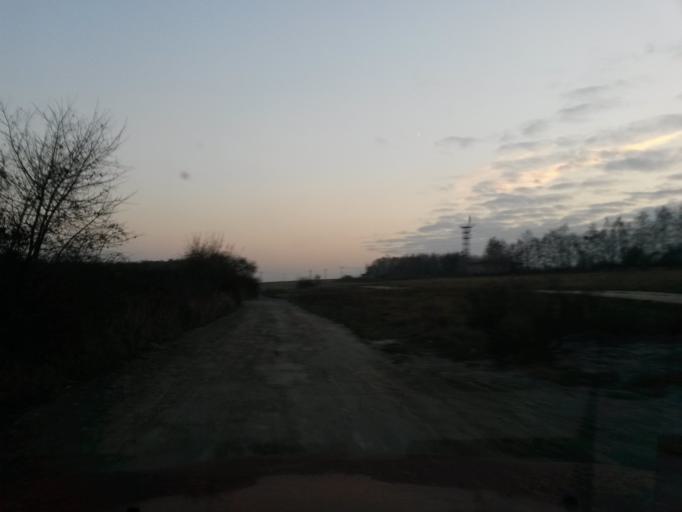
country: SK
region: Kosicky
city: Kosice
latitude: 48.7171
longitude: 21.2935
